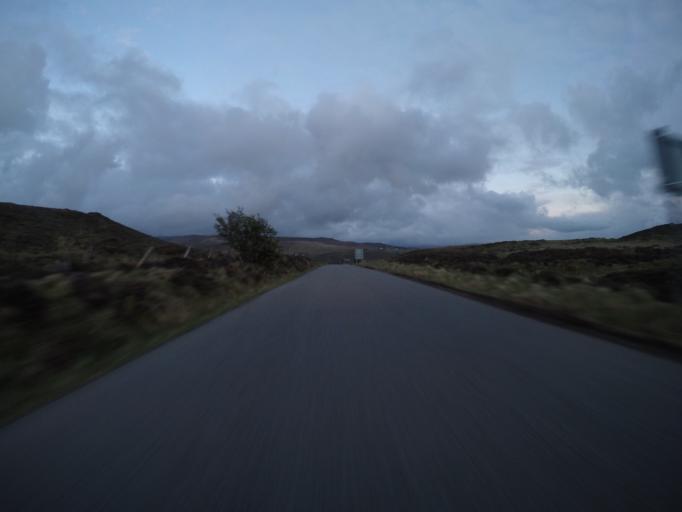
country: GB
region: Scotland
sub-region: Highland
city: Portree
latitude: 57.5953
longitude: -6.3742
